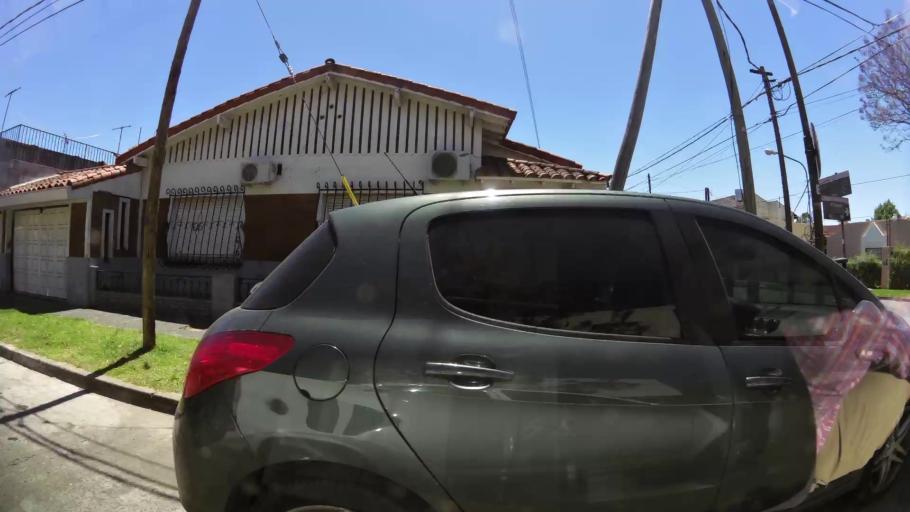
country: AR
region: Buenos Aires
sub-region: Partido de Vicente Lopez
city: Olivos
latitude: -34.5178
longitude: -58.5395
